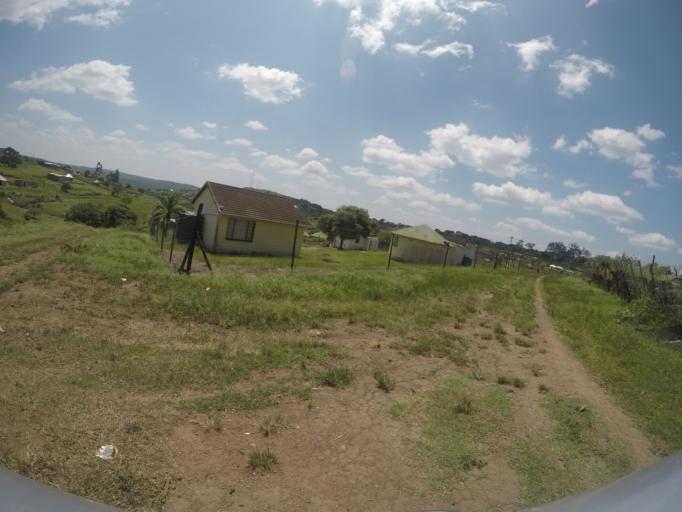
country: ZA
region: KwaZulu-Natal
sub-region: uThungulu District Municipality
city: Empangeni
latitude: -28.6061
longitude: 31.7375
